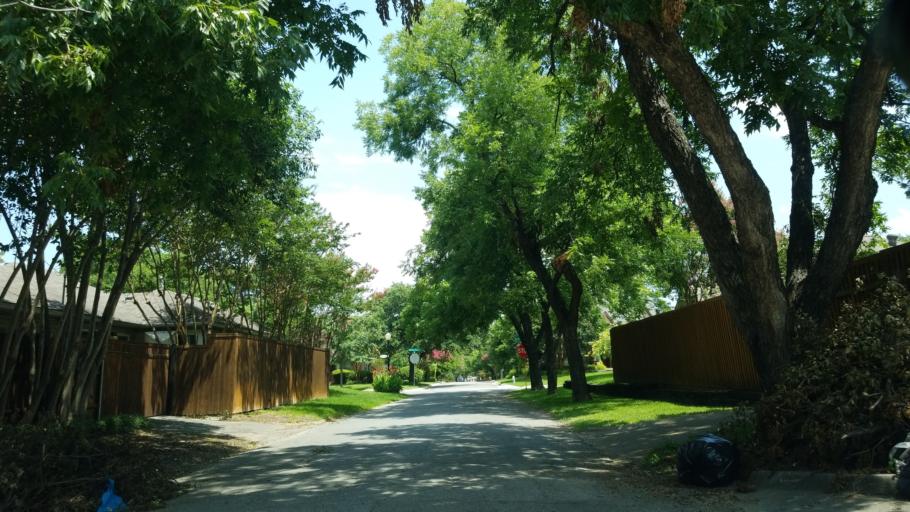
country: US
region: Texas
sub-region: Dallas County
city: Highland Park
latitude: 32.8240
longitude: -96.7799
